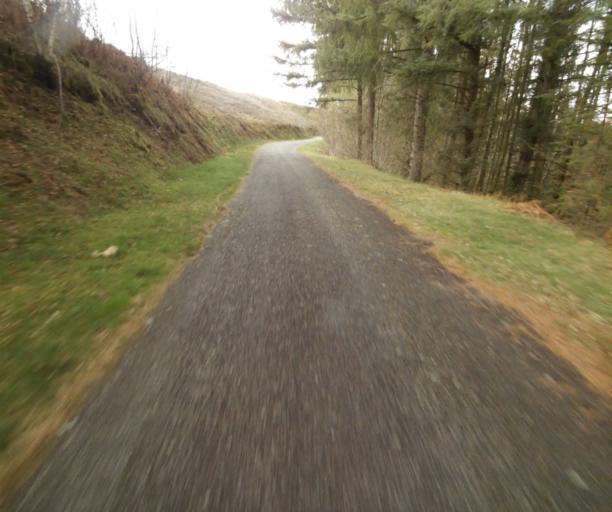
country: FR
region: Limousin
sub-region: Departement de la Correze
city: Egletons
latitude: 45.2742
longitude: 1.9953
